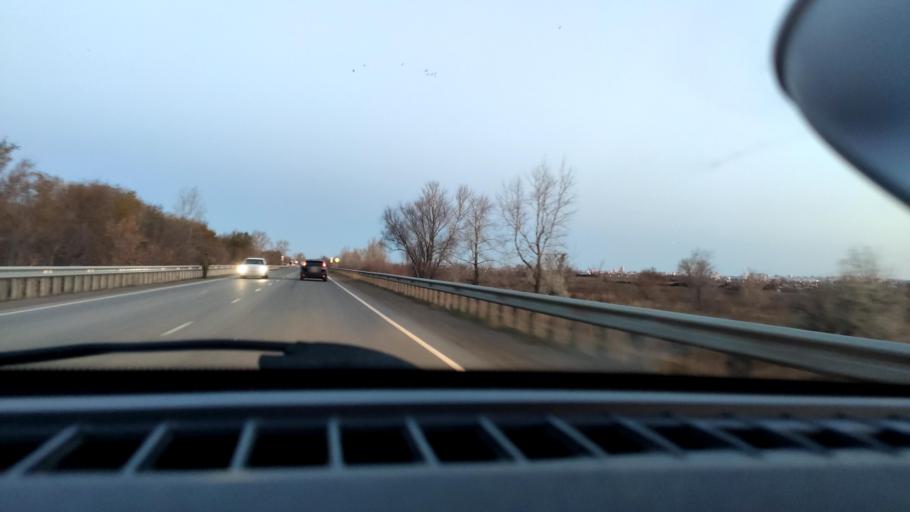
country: RU
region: Samara
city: Samara
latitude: 53.1102
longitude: 50.1303
